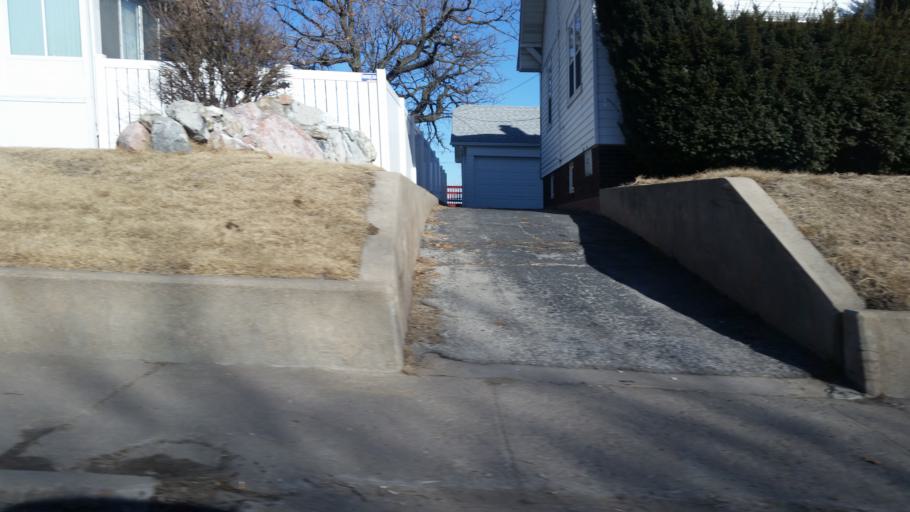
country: US
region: Nebraska
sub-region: Douglas County
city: Omaha
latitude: 41.1941
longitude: -95.9335
